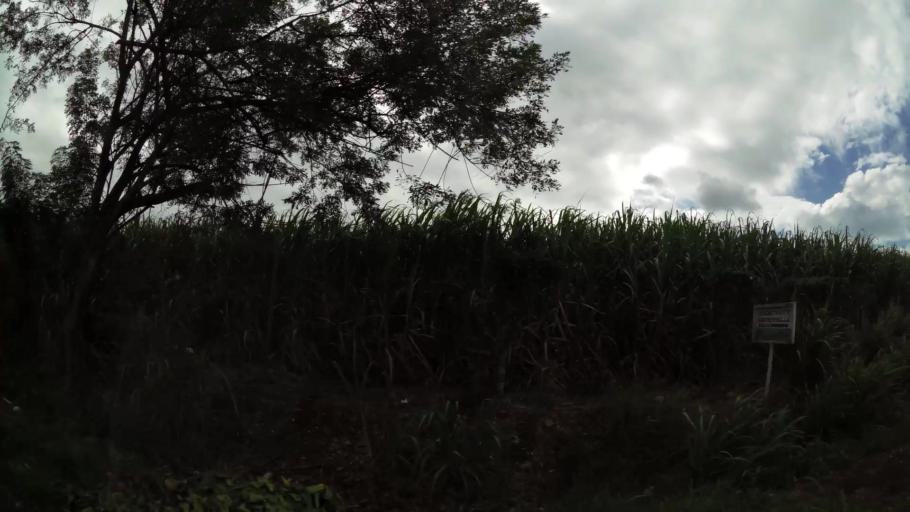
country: GP
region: Guadeloupe
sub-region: Guadeloupe
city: Sainte-Rose
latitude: 16.3241
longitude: -61.6990
